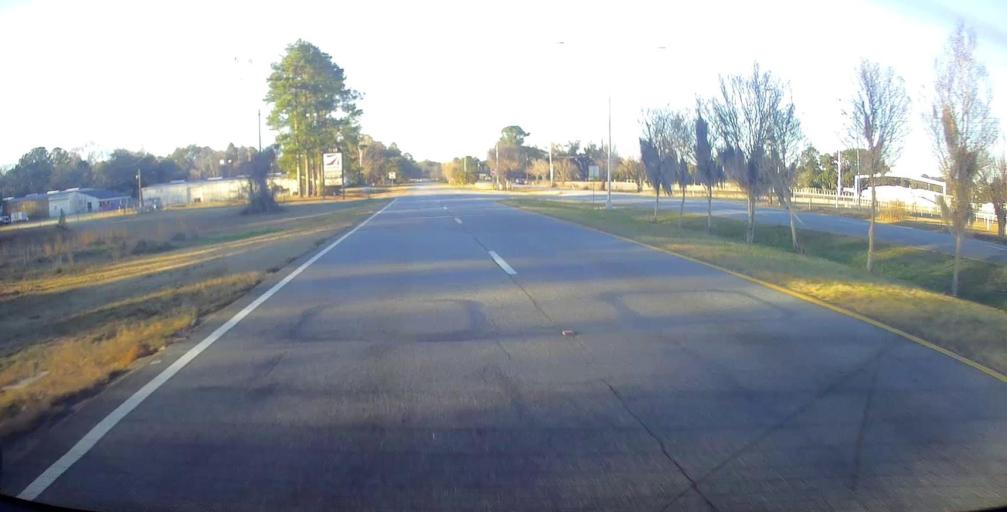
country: US
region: Georgia
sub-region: Dougherty County
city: Albany
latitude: 31.5501
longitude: -84.2245
